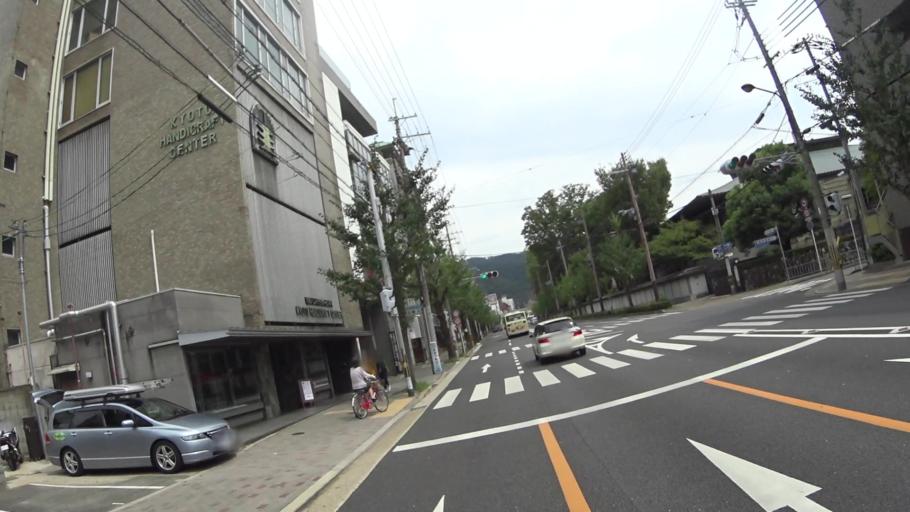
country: JP
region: Kyoto
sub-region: Kyoto-shi
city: Kamigyo-ku
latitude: 35.0174
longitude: 135.7800
